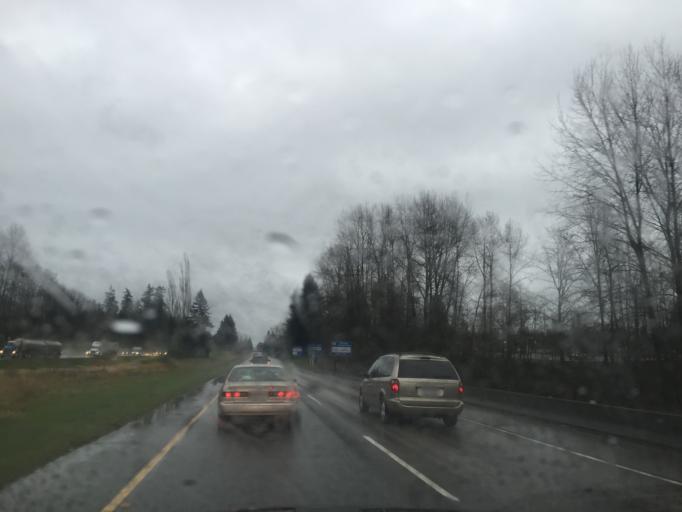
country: CA
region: British Columbia
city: Walnut Grove
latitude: 49.1437
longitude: -122.6007
